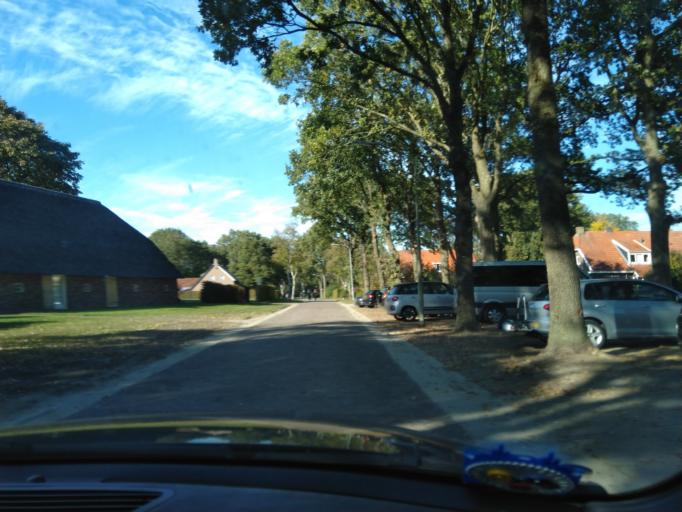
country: NL
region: Drenthe
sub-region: Gemeente Aa en Hunze
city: Anloo
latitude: 53.0368
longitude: 6.6641
